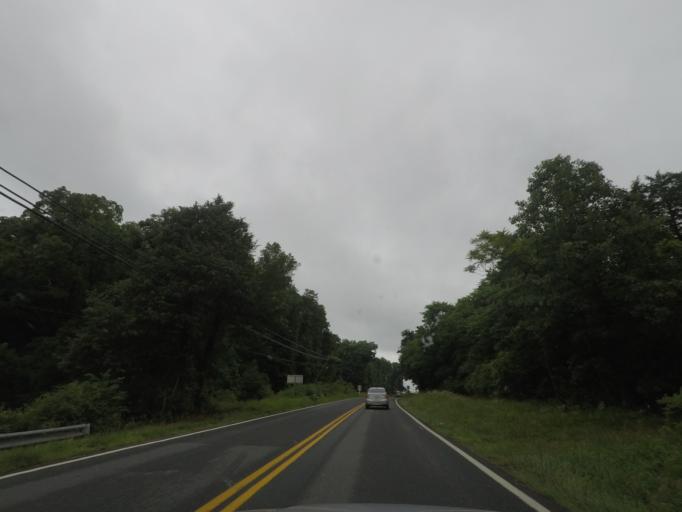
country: US
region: Virginia
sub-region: Fluvanna County
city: Palmyra
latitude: 37.8646
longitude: -78.2633
